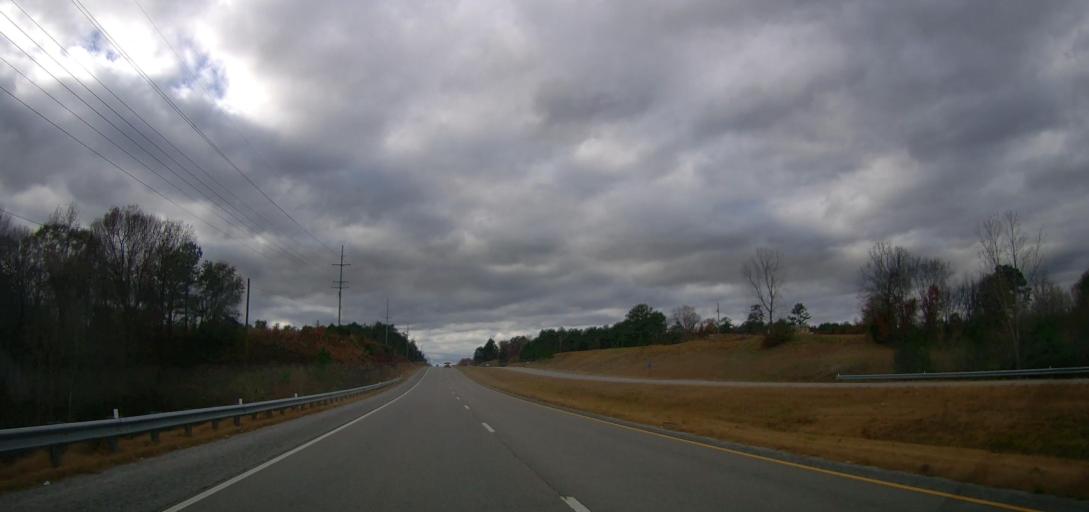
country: US
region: Alabama
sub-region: Lawrence County
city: Moulton
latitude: 34.5636
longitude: -87.3585
